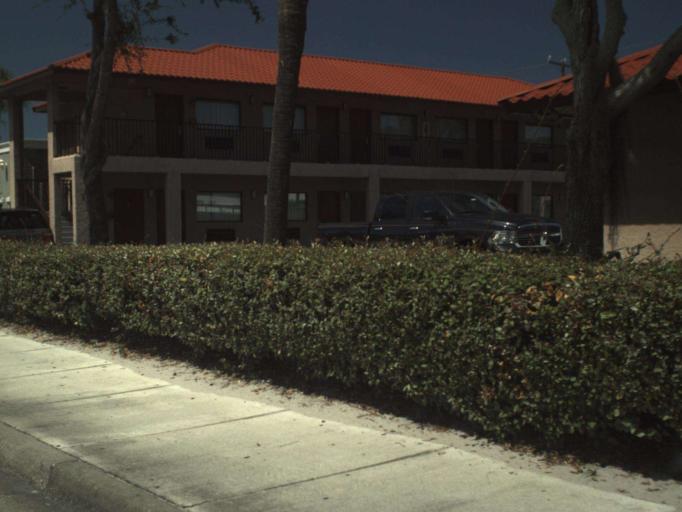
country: US
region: Florida
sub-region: Saint Lucie County
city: Fort Pierce
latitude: 27.4412
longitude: -80.3258
